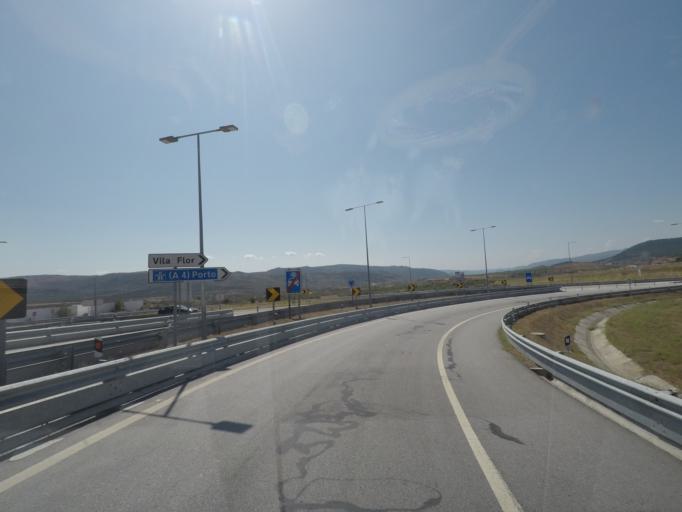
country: PT
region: Braganca
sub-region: Braganca Municipality
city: Vila Flor
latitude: 41.3254
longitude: -7.0775
